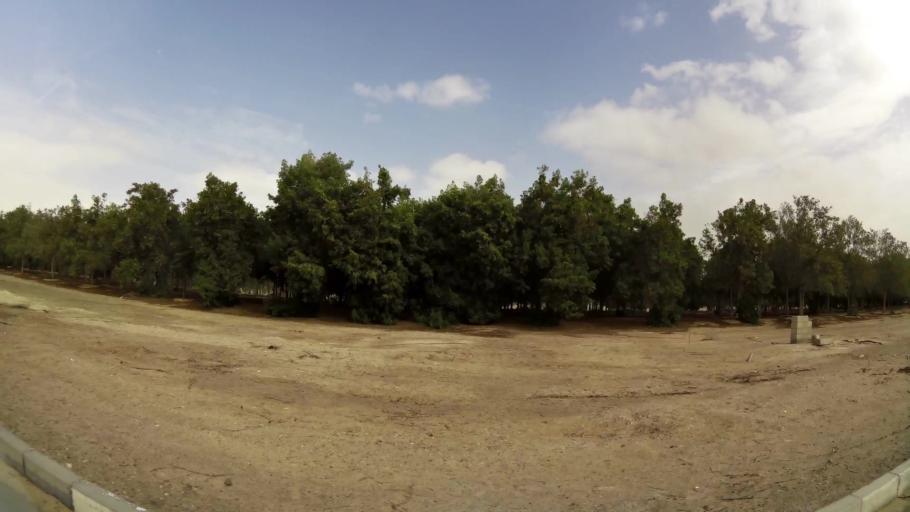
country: AE
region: Abu Dhabi
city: Abu Dhabi
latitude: 24.4004
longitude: 54.4906
